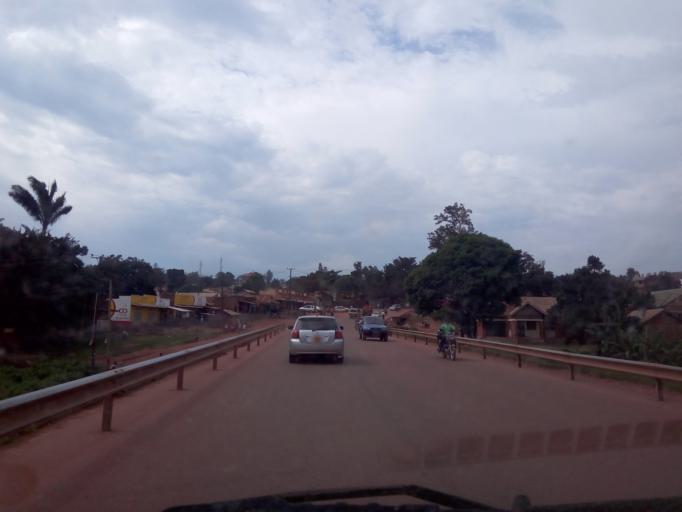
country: UG
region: Central Region
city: Kampala Central Division
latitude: 0.3509
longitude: 32.5797
